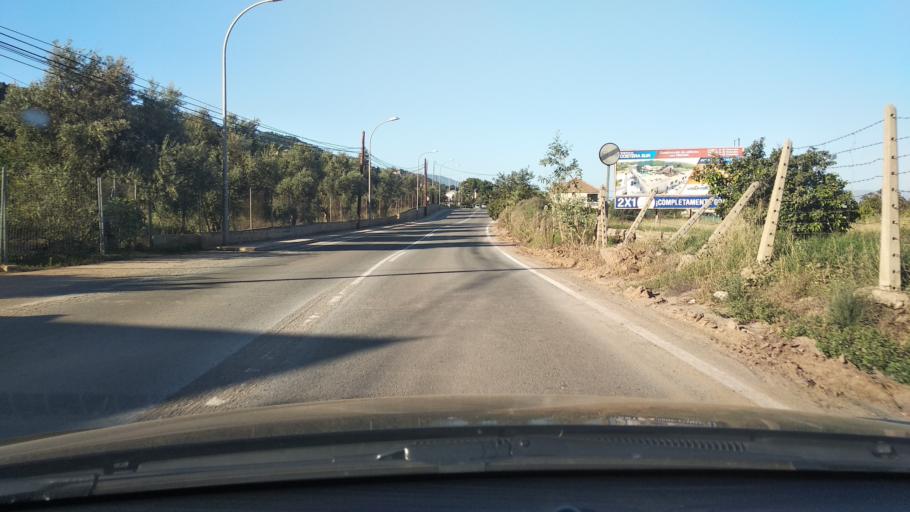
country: ES
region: Murcia
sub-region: Murcia
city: Murcia
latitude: 37.9480
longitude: -1.1045
